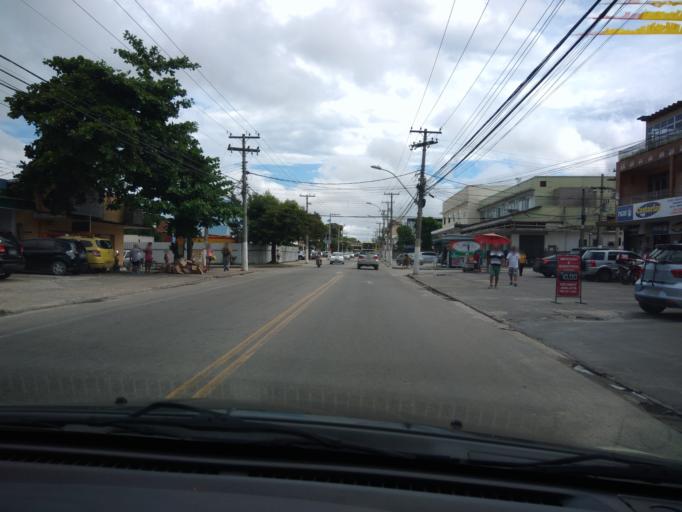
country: BR
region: Rio de Janeiro
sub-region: Niteroi
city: Niteroi
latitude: -22.9434
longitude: -43.0299
